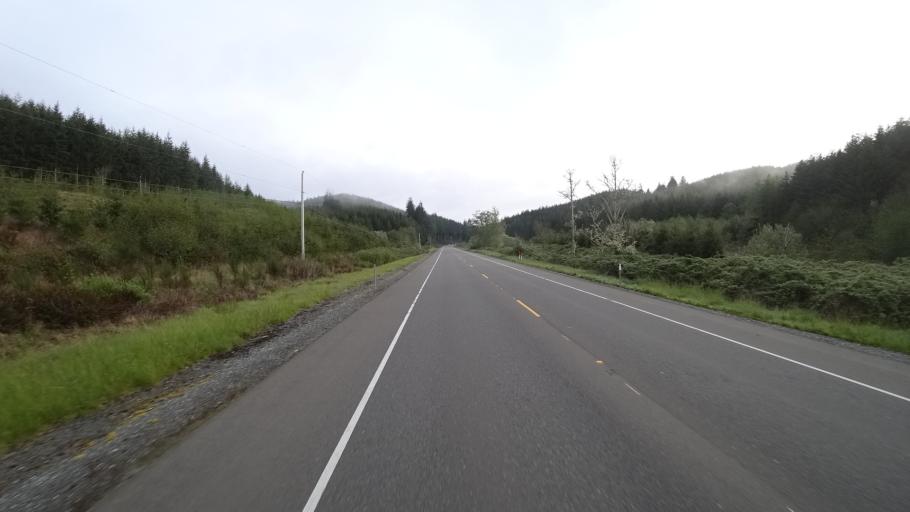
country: US
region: Oregon
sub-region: Coos County
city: Barview
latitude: 43.2782
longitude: -124.2595
